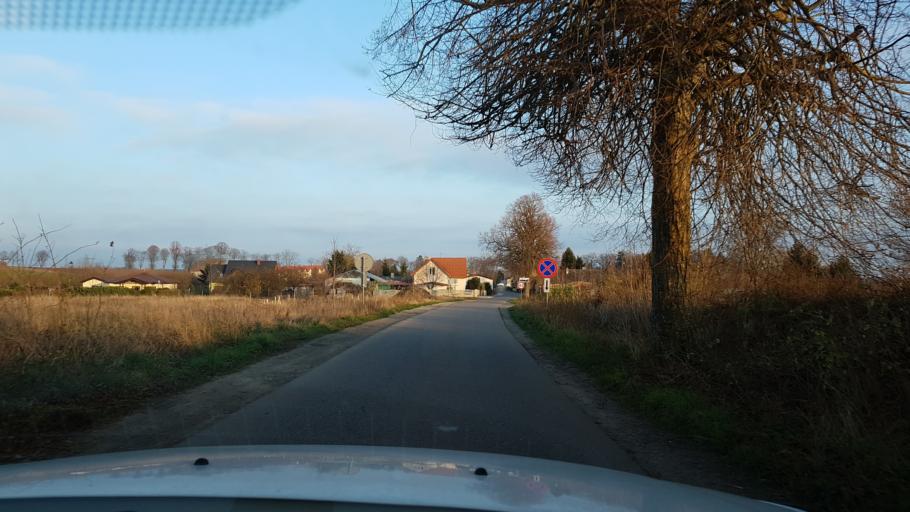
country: PL
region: West Pomeranian Voivodeship
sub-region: Powiat koszalinski
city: Mielno
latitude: 54.1403
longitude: 16.0590
